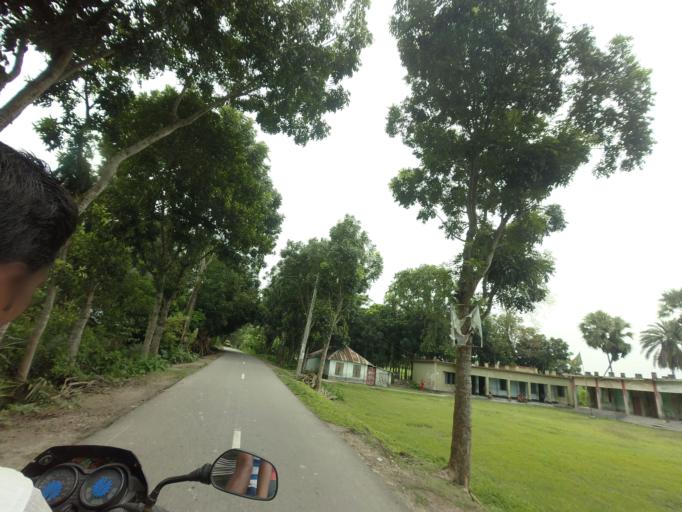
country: BD
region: Khulna
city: Kalia
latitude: 23.1087
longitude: 89.6470
